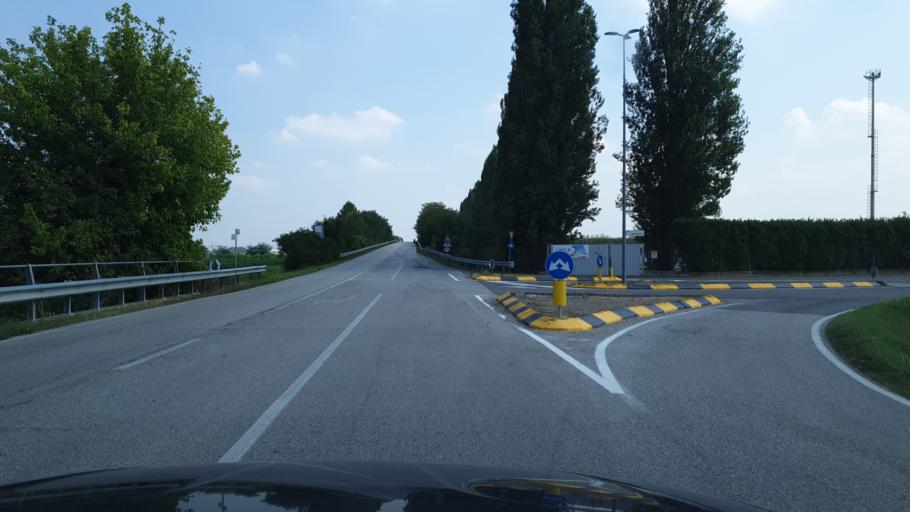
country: IT
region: Veneto
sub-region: Provincia di Rovigo
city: Arqua Polesine
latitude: 45.0115
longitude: 11.7459
